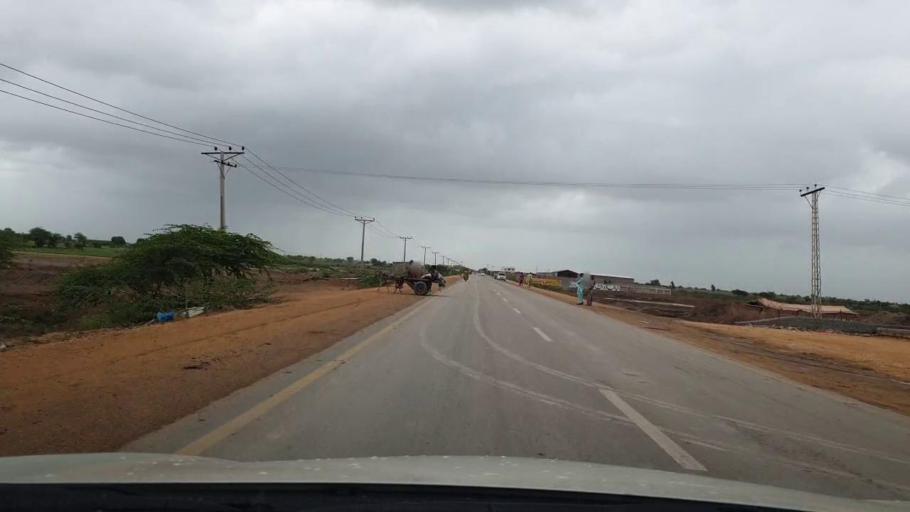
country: PK
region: Sindh
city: Badin
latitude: 24.6536
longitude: 68.7664
